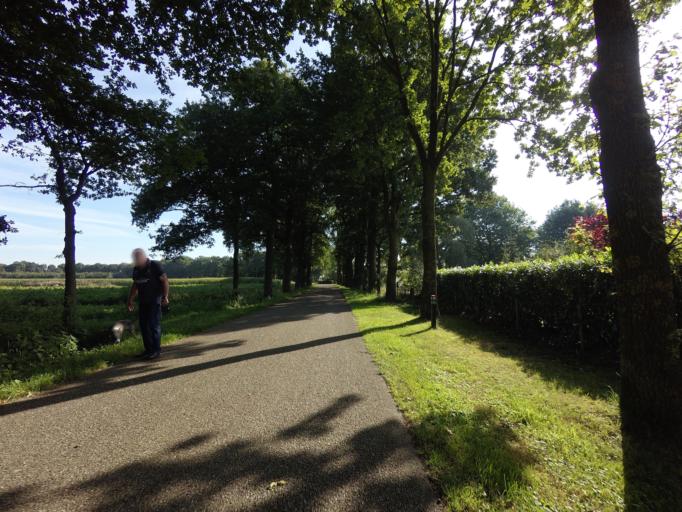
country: NL
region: Gelderland
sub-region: Oude IJsselstreek
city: Varsseveld
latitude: 51.9470
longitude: 6.4665
